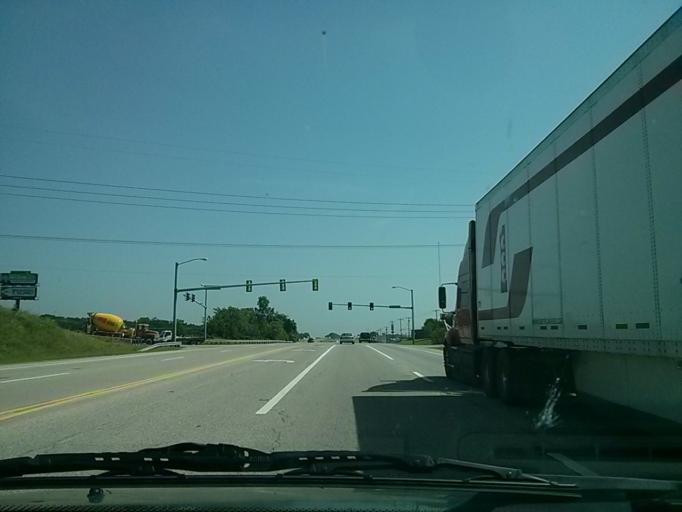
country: US
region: Oklahoma
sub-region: Tulsa County
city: Oakhurst
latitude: 36.0458
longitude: -96.0788
